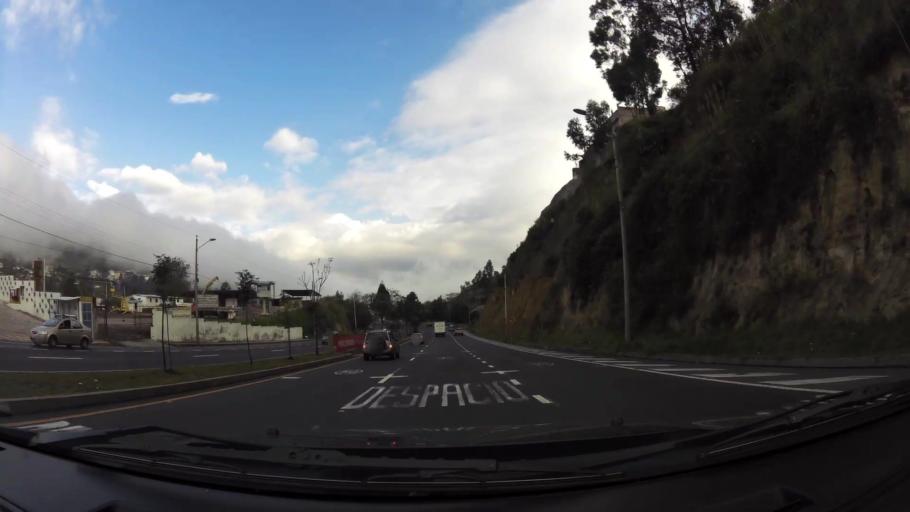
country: EC
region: Pichincha
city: Quito
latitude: -0.2350
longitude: -78.4883
